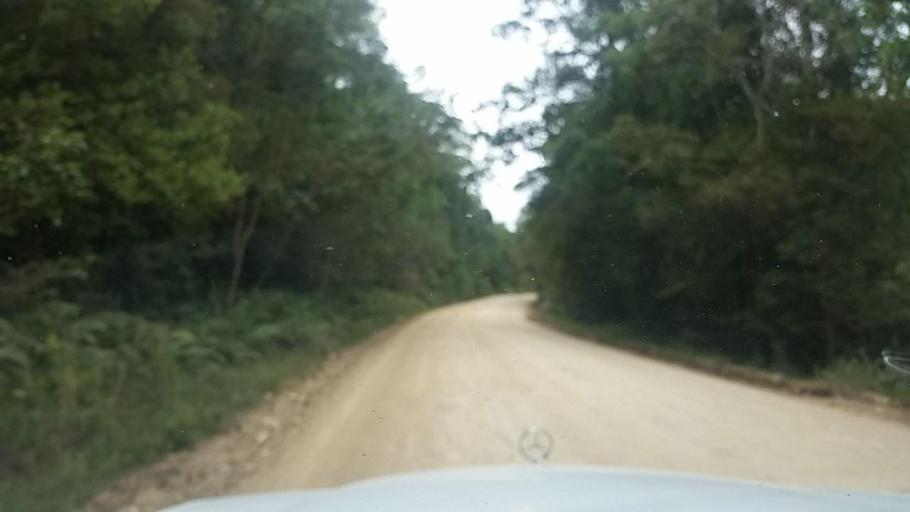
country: ZA
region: Western Cape
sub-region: Eden District Municipality
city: Knysna
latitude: -33.9588
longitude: 23.1571
